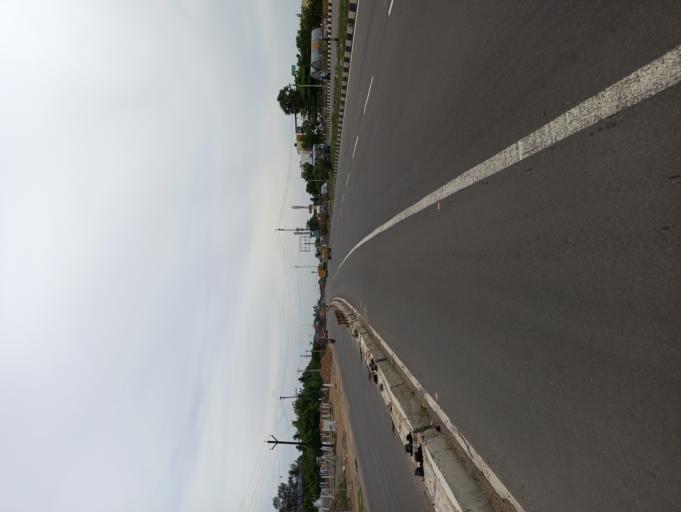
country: IN
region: Tamil Nadu
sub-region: Kancheepuram
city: Poonamalle
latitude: 13.0572
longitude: 80.1010
